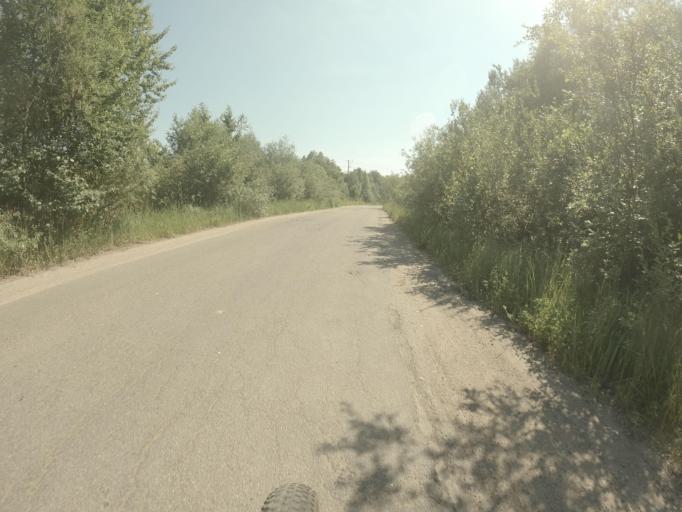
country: RU
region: St.-Petersburg
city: Obukhovo
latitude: 59.8366
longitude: 30.4735
